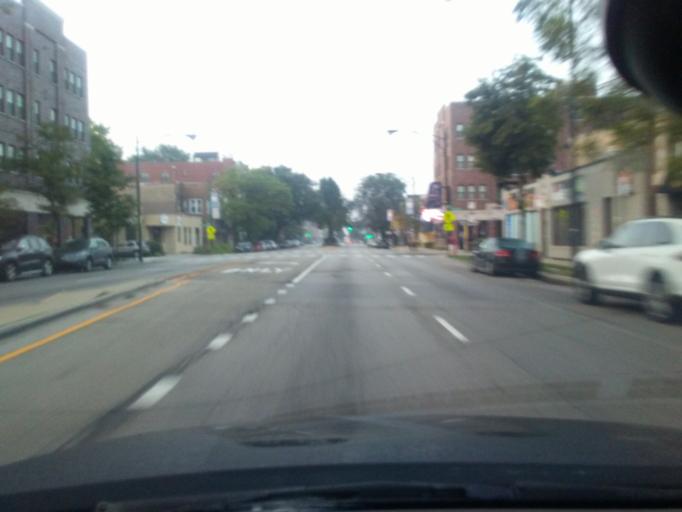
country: US
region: Illinois
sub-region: Cook County
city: Lincolnwood
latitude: 41.9493
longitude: -87.6690
